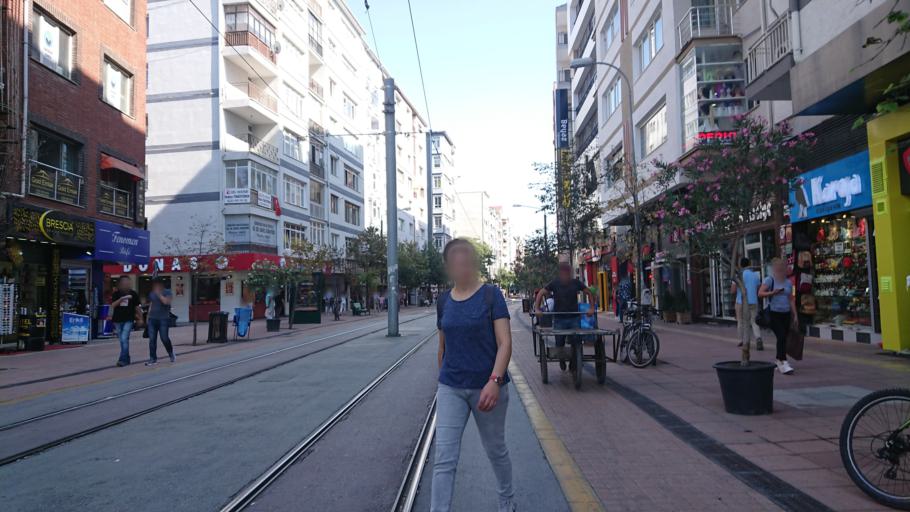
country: TR
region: Eskisehir
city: Eskisehir
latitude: 39.7799
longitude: 30.5127
